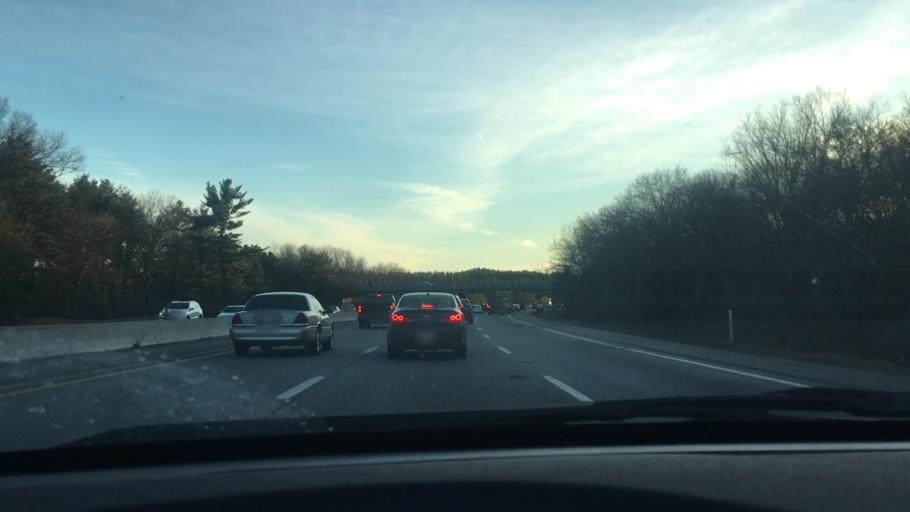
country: US
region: Massachusetts
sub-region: Middlesex County
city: Cochituate
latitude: 42.3215
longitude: -71.3408
